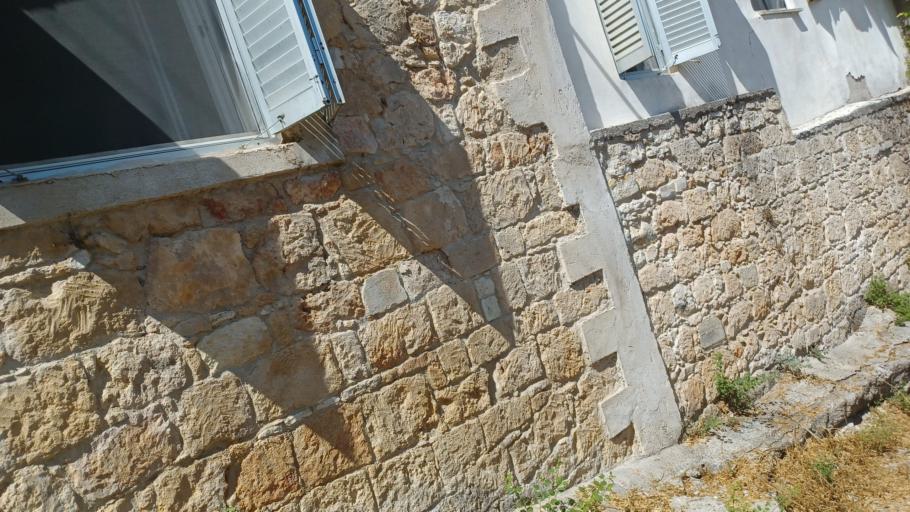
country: CY
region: Pafos
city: Tala
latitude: 34.8600
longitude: 32.4558
